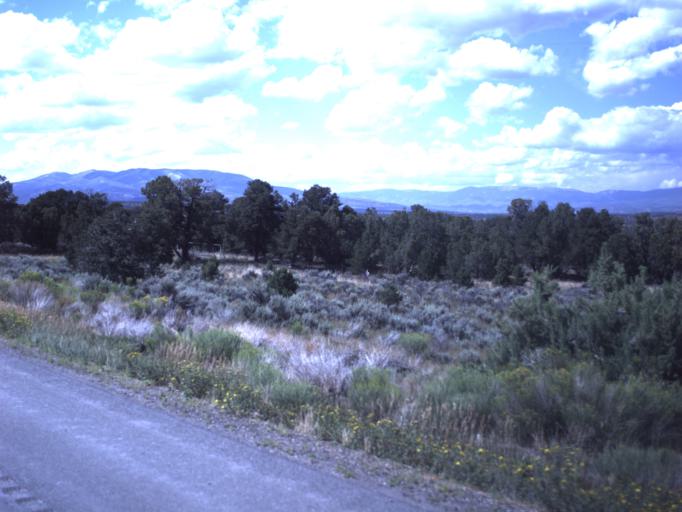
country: US
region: Utah
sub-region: Duchesne County
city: Duchesne
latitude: 40.1914
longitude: -110.6801
